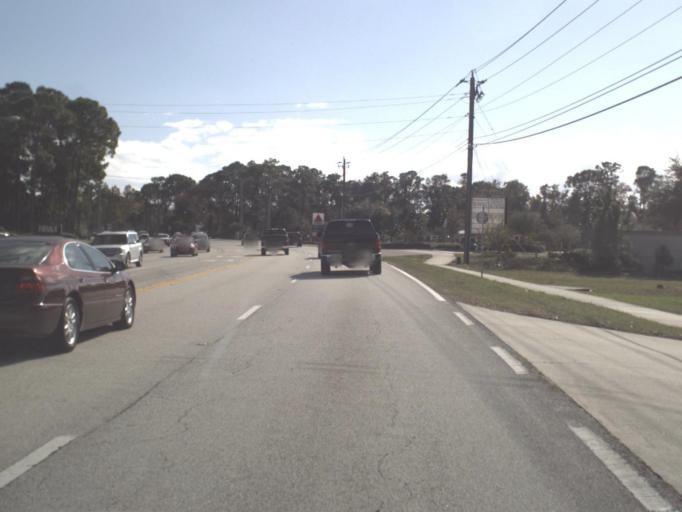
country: US
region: Florida
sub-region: Volusia County
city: South Daytona
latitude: 29.1582
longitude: -81.0388
